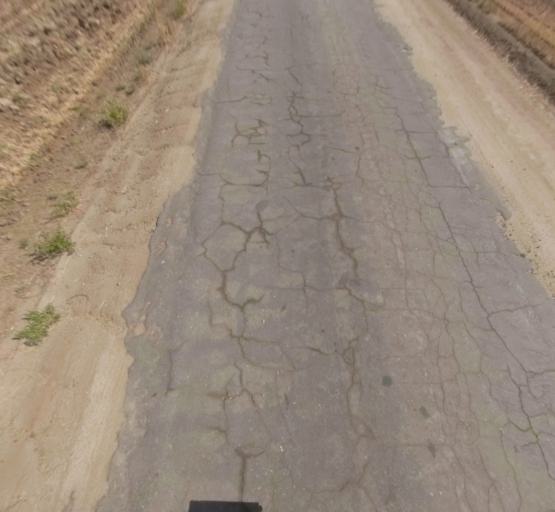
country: US
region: California
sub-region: Madera County
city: Chowchilla
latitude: 37.1319
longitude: -120.2926
